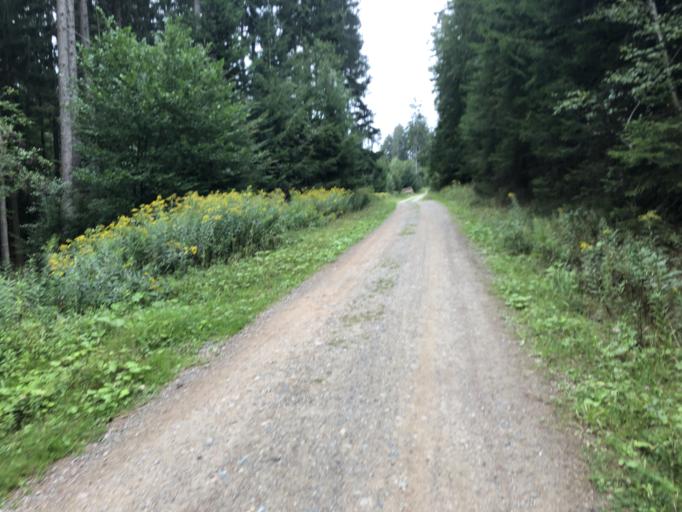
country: DE
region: Hesse
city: Unter-Abtsteinach
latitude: 49.5408
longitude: 8.7992
